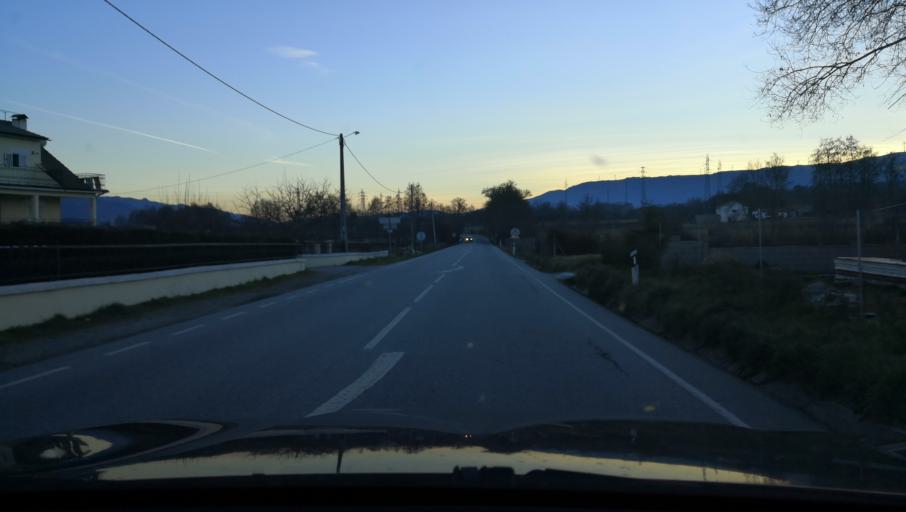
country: PT
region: Vila Real
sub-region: Vila Pouca de Aguiar
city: Vila Pouca de Aguiar
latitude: 41.4691
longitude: -7.6637
